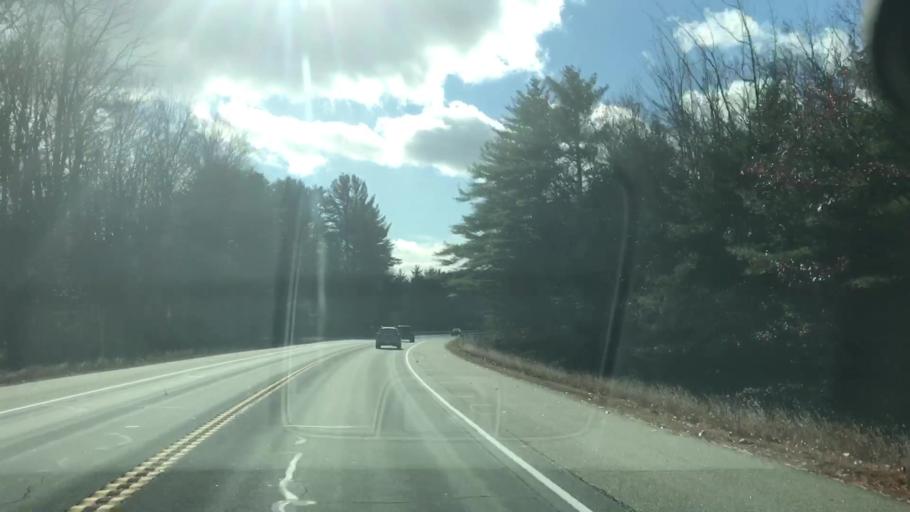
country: US
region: New Hampshire
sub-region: Carroll County
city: Wolfeboro
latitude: 43.5108
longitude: -71.2142
